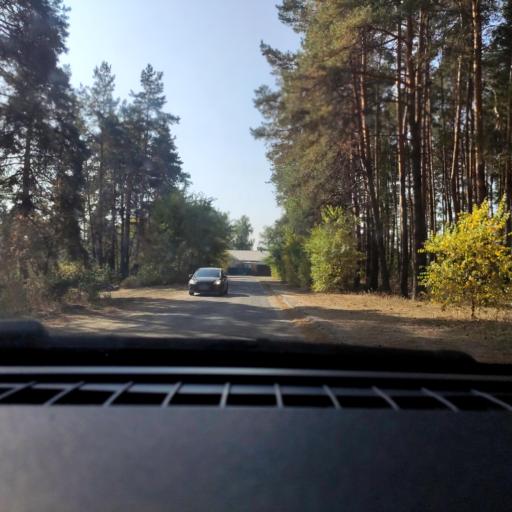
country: RU
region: Voronezj
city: Maslovka
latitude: 51.5475
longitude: 39.2213
